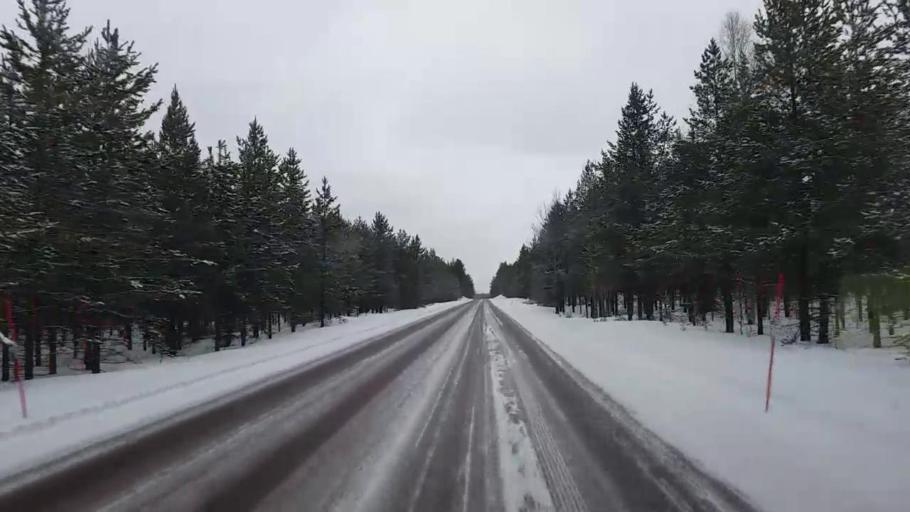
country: SE
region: Jaemtland
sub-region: Bergs Kommun
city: Hoverberg
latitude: 62.4447
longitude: 14.5717
